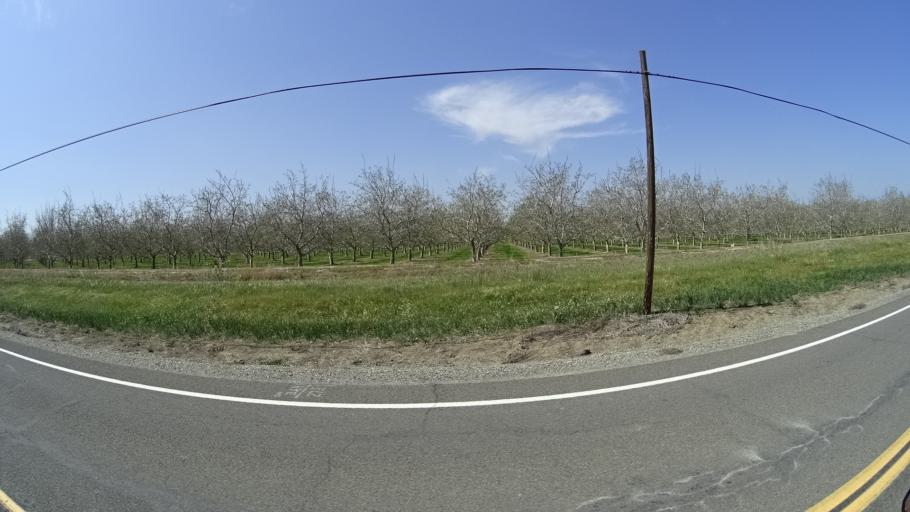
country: US
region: California
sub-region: Glenn County
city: Willows
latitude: 39.4670
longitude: -122.0194
